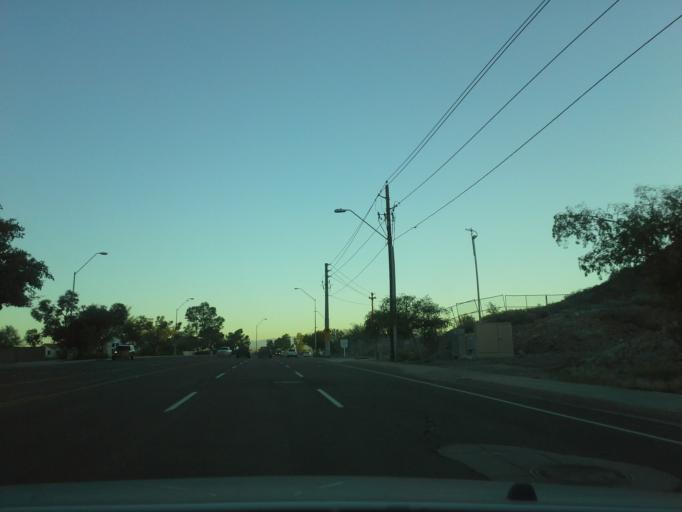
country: US
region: Arizona
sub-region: Maricopa County
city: Paradise Valley
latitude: 33.6146
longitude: -112.0347
